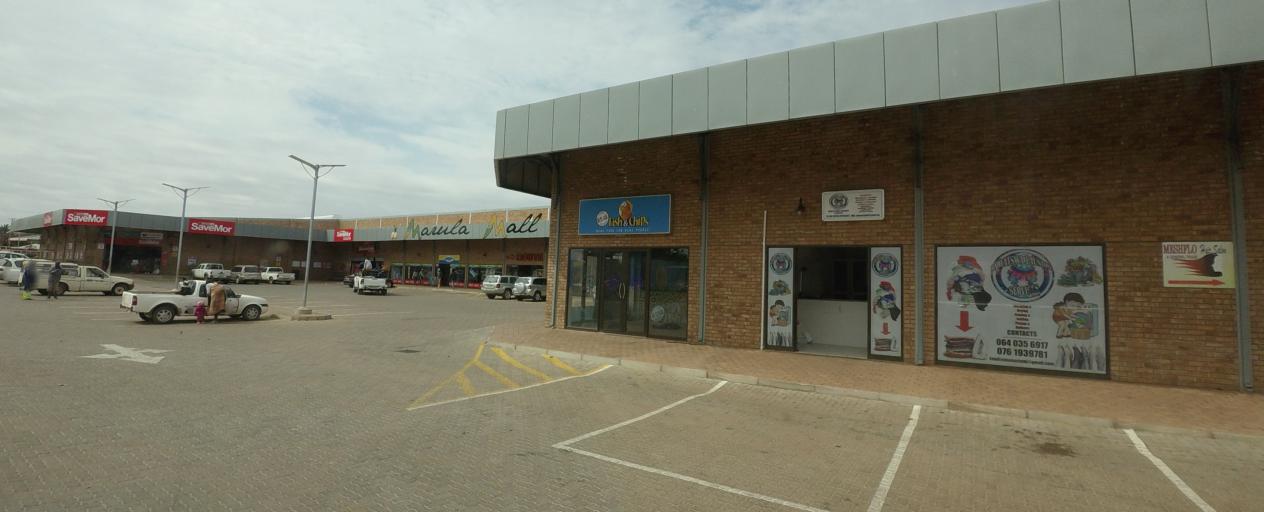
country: BW
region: Central
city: Mathathane
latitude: -22.6801
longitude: 29.1066
